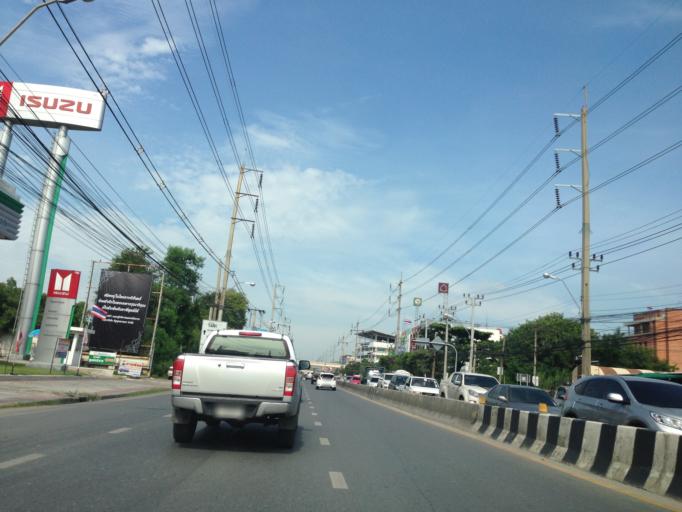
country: TH
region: Phra Nakhon Si Ayutthaya
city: Ban Bang Kadi Pathum Thani
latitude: 13.9458
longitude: 100.5448
